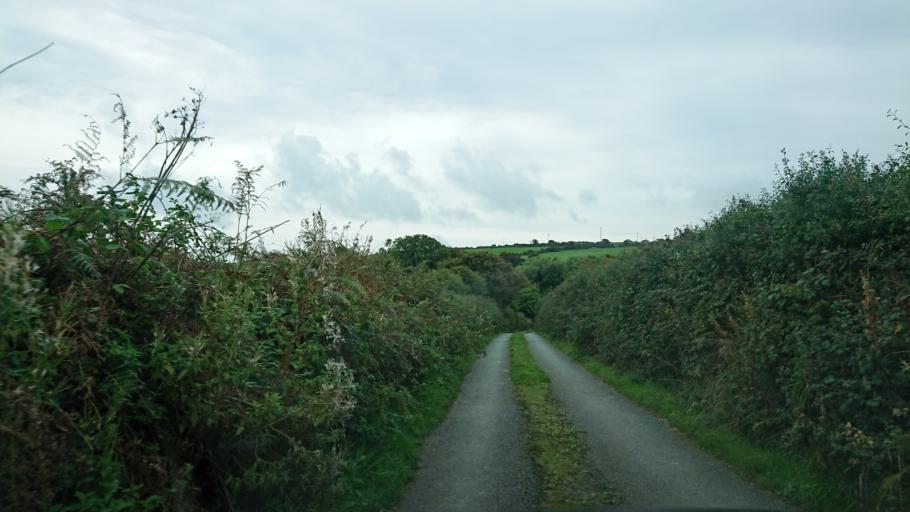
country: IE
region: Munster
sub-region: Waterford
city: Dunmore East
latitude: 52.1727
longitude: -6.9954
